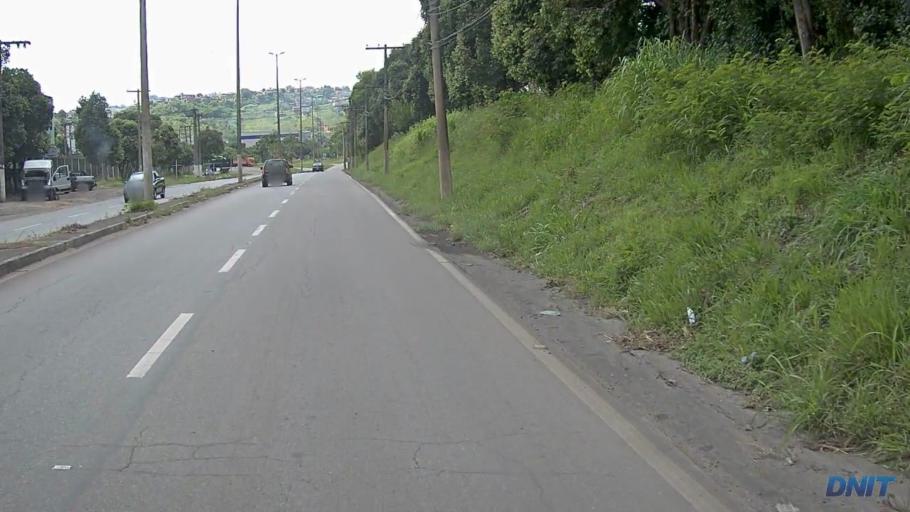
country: BR
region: Minas Gerais
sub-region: Coronel Fabriciano
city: Coronel Fabriciano
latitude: -19.5282
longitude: -42.6453
